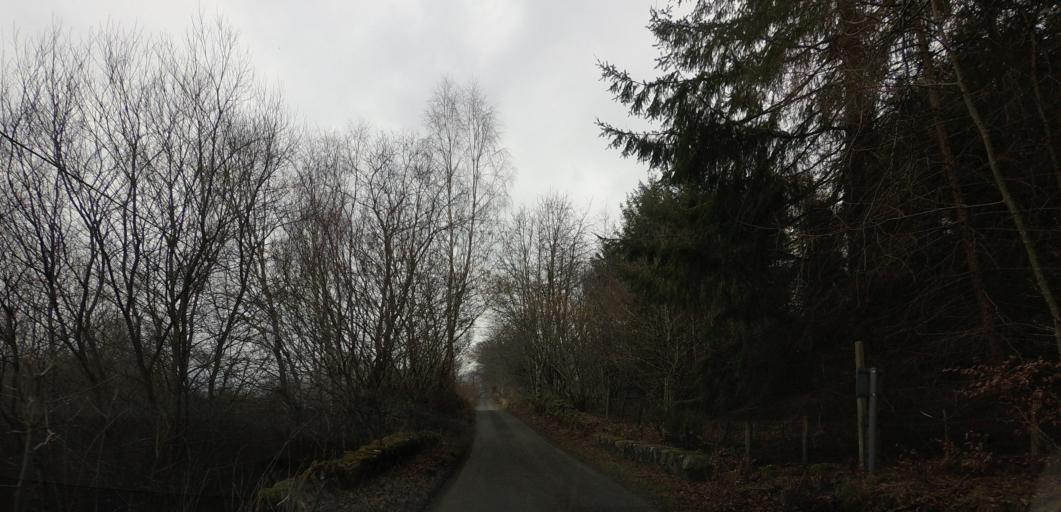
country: GB
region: Scotland
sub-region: Perth and Kinross
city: Comrie
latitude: 56.5178
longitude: -4.1248
